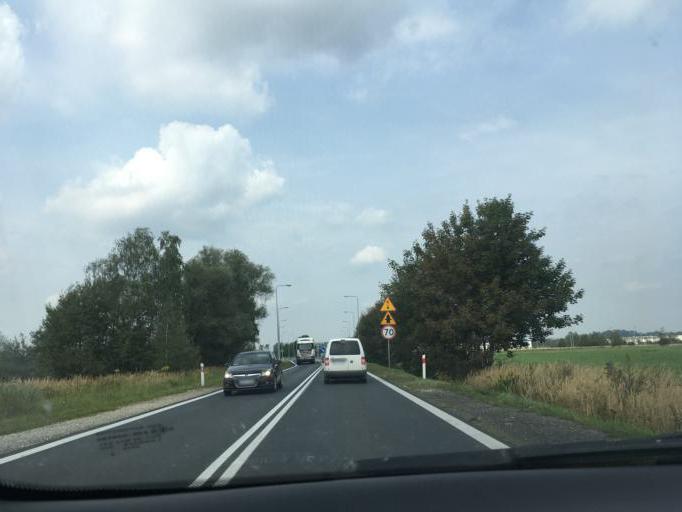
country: PL
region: Silesian Voivodeship
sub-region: Powiat bierunsko-ledzinski
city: Bierun
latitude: 50.0901
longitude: 19.1065
